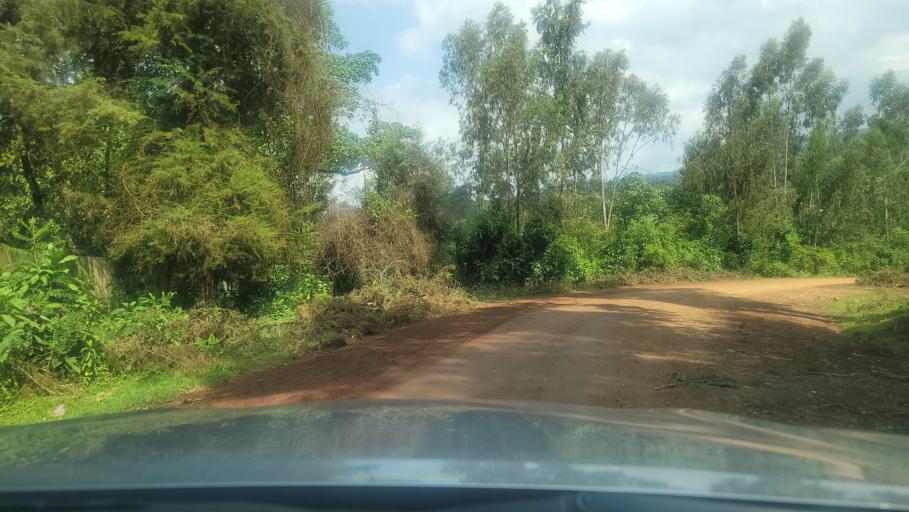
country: ET
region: Oromiya
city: Agaro
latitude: 7.7850
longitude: 36.4271
